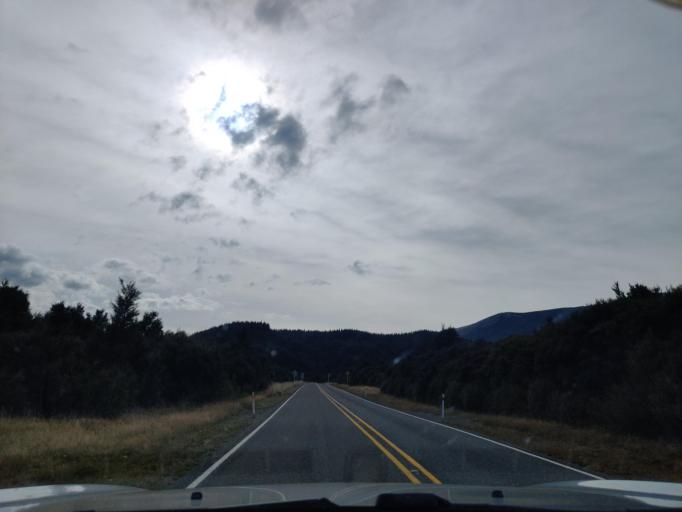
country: NZ
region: Tasman
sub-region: Tasman District
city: Wakefield
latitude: -41.7151
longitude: 173.0832
